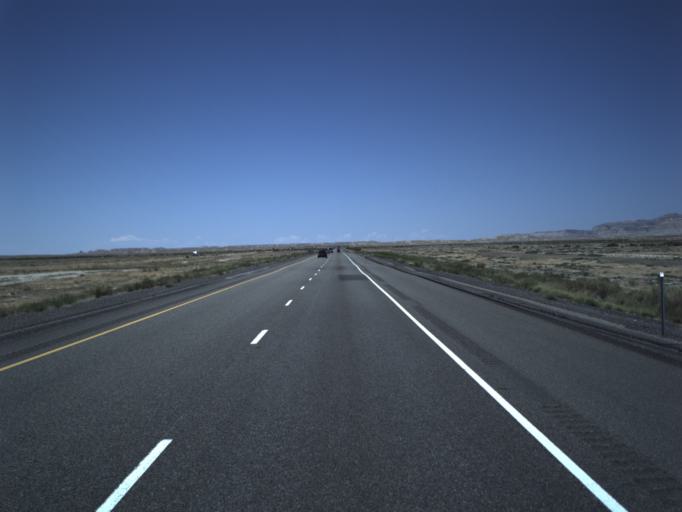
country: US
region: Utah
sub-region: Grand County
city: Moab
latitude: 38.9428
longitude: -109.5726
